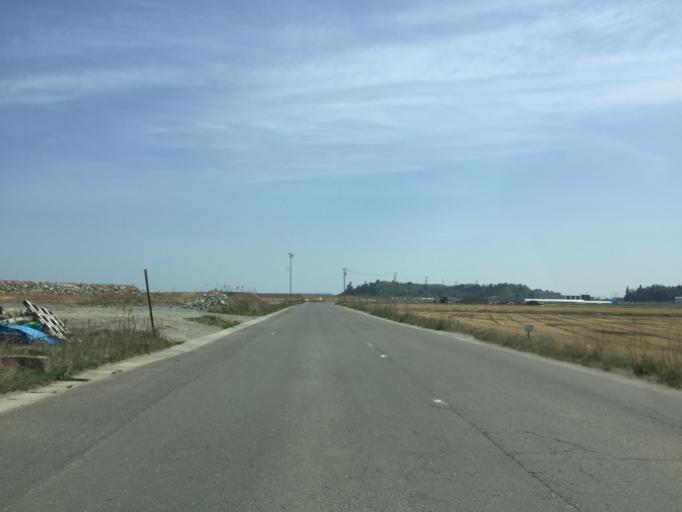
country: JP
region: Miyagi
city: Watari
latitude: 37.9080
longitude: 140.9215
